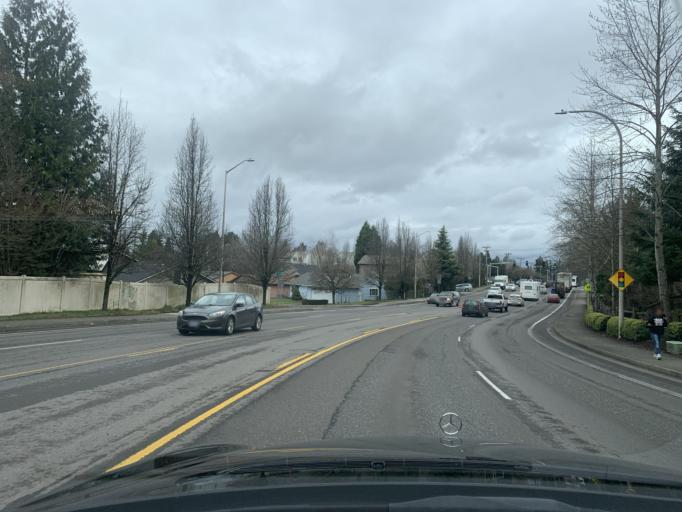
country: US
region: Oregon
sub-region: Multnomah County
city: Gresham
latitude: 45.4904
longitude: -122.3987
